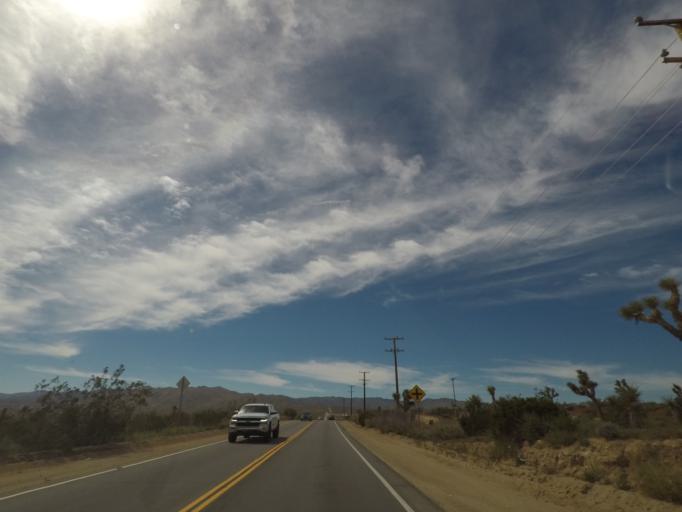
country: US
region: California
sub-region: San Bernardino County
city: Joshua Tree
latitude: 34.1506
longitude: -116.3696
